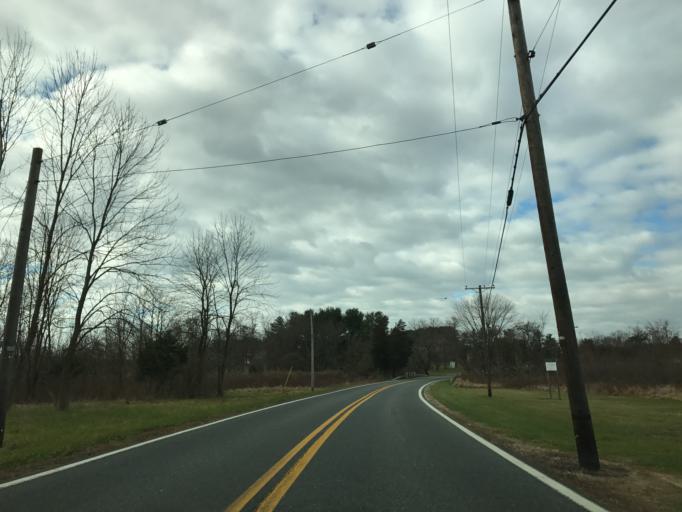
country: US
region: Maryland
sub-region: Baltimore County
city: Perry Hall
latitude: 39.4834
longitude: -76.4884
